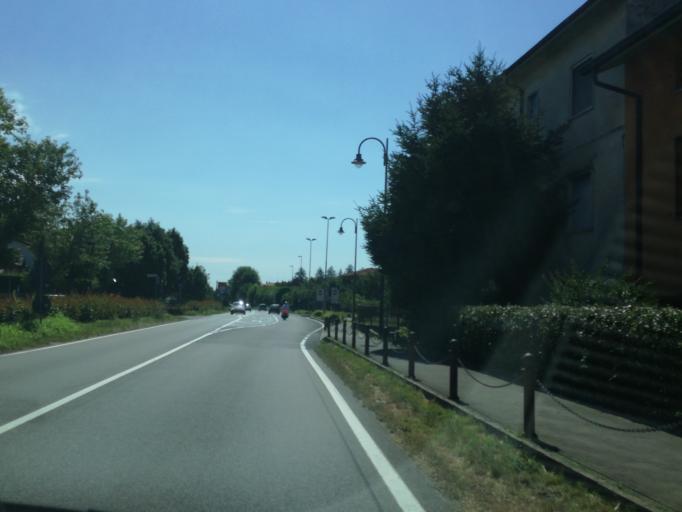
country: IT
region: Lombardy
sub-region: Provincia di Bergamo
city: Terno d'Isola
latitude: 45.6912
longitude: 9.5190
